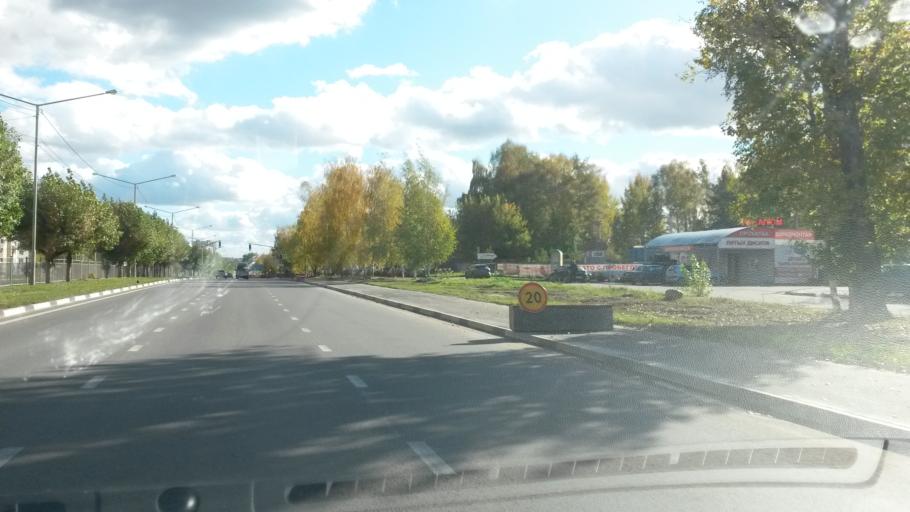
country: RU
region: Jaroslavl
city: Yaroslavl
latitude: 57.5786
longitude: 39.9140
